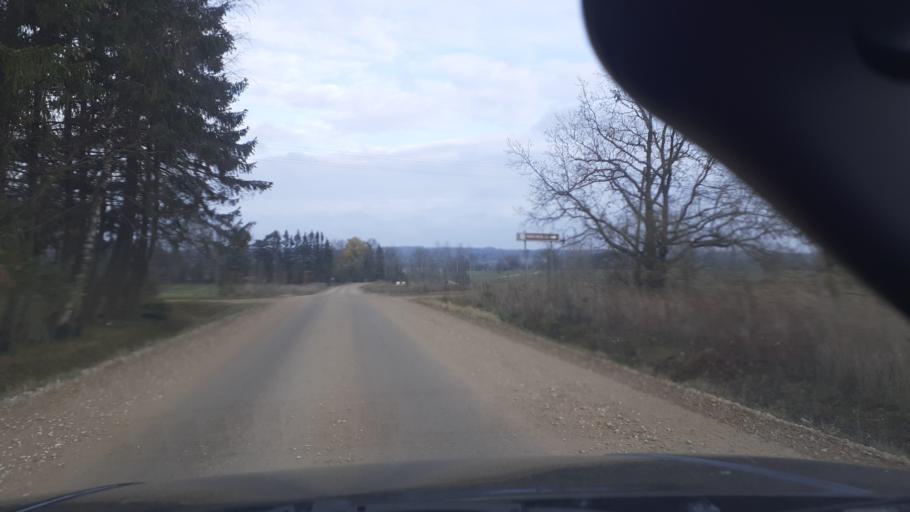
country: LV
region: Aizpute
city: Aizpute
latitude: 56.8624
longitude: 21.6715
